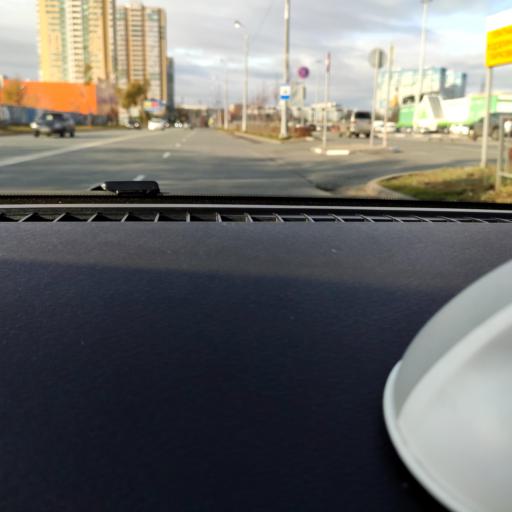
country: RU
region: Samara
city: Samara
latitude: 53.2081
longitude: 50.1966
